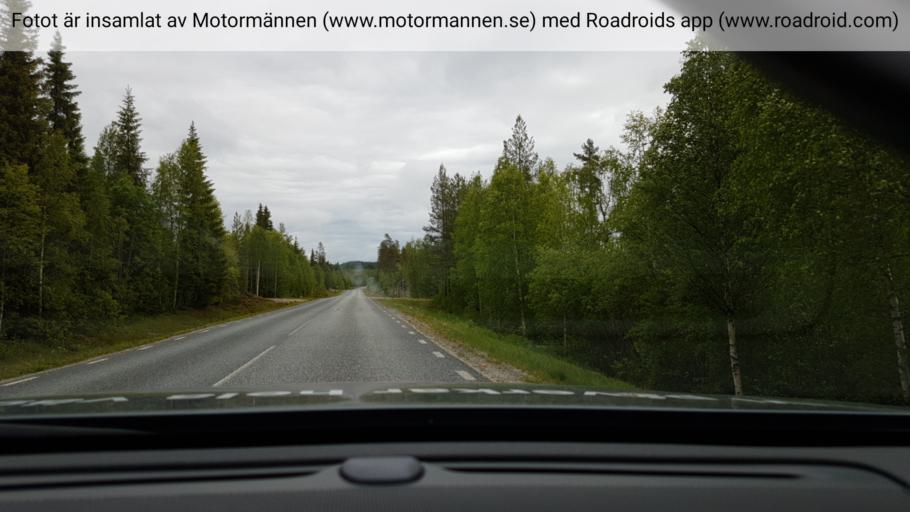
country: SE
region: Vaesterbotten
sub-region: Asele Kommun
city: Insjon
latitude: 64.3374
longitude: 17.7602
